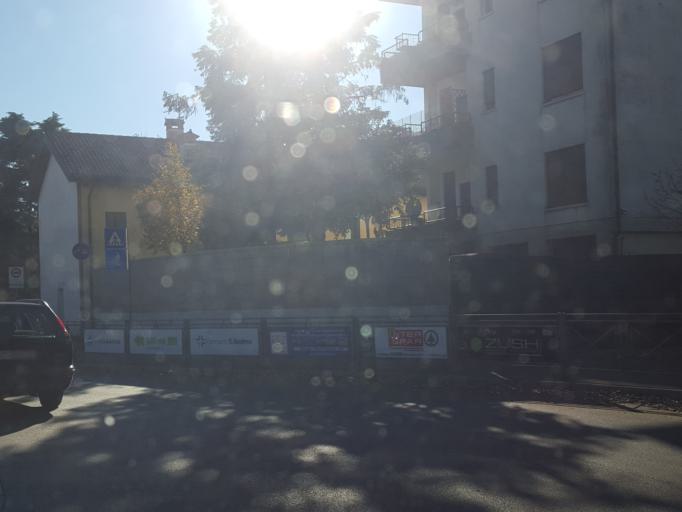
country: IT
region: Veneto
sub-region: Provincia di Vicenza
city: Vicenza
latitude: 45.5535
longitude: 11.5640
